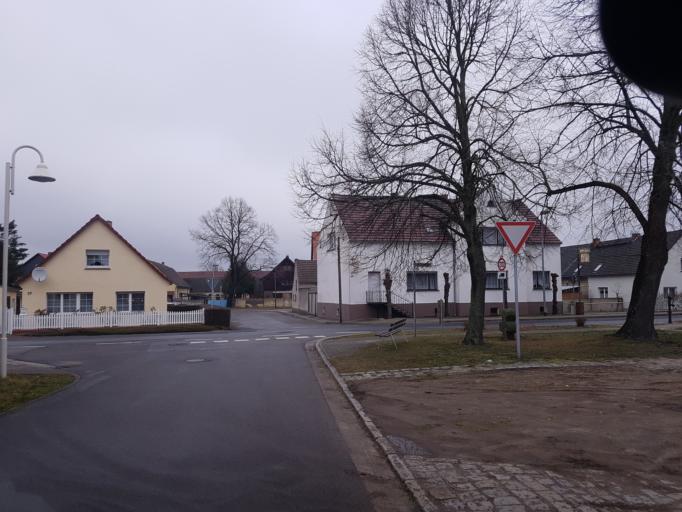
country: DE
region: Brandenburg
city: Plessa
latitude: 51.5340
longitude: 13.6287
